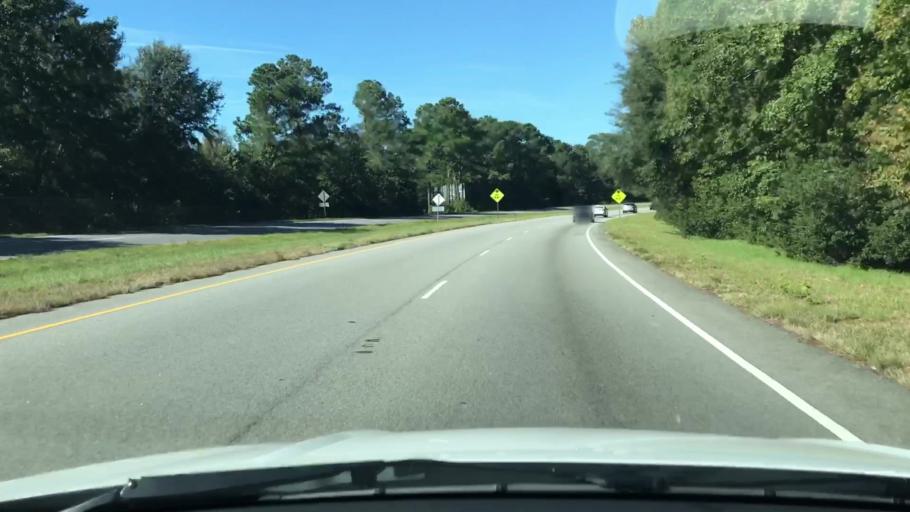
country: US
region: South Carolina
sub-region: Beaufort County
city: Laurel Bay
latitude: 32.5130
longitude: -80.7514
